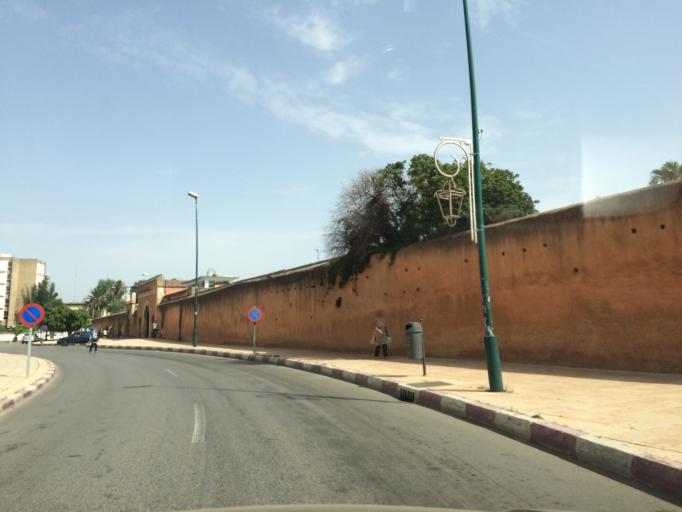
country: MA
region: Rabat-Sale-Zemmour-Zaer
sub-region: Rabat
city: Rabat
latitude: 34.0131
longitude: -6.8335
